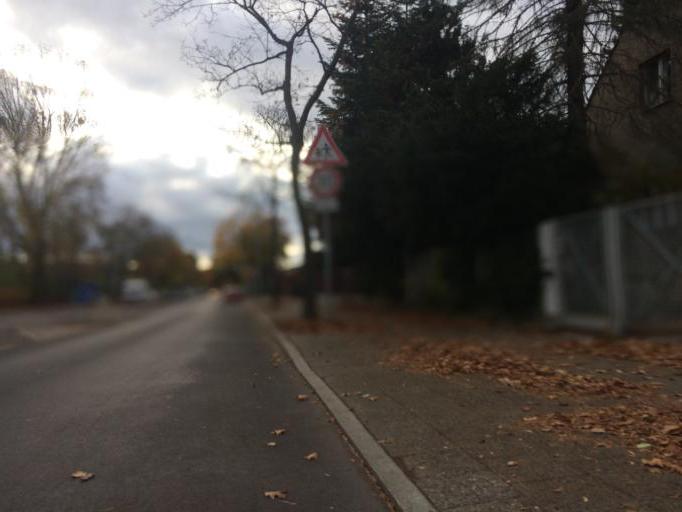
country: DE
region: Berlin
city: Lubars
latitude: 52.6067
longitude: 13.3402
